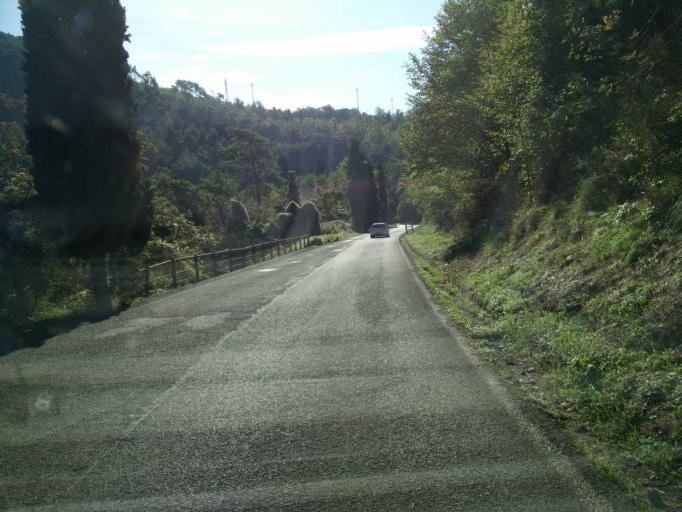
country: IT
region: Liguria
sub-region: Provincia di La Spezia
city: Framura
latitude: 44.2148
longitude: 9.5597
